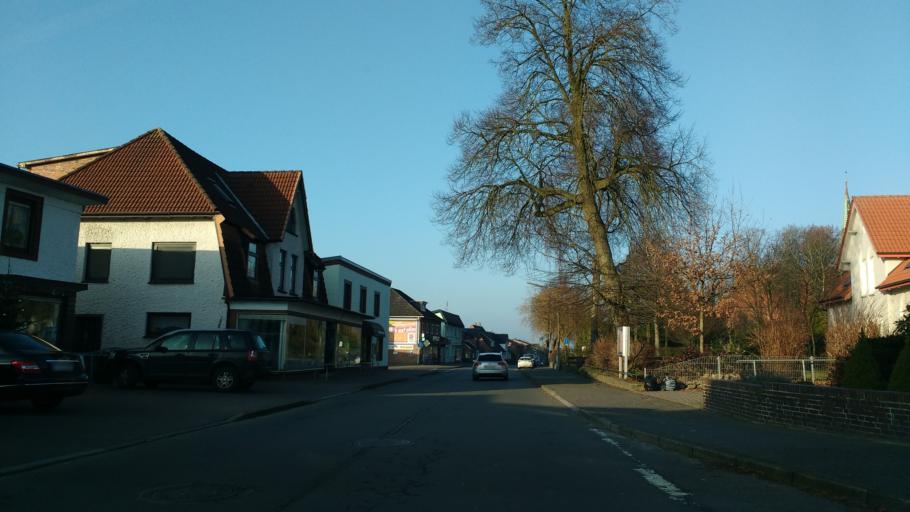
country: DE
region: Schleswig-Holstein
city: Wacken
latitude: 54.0202
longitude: 9.3755
